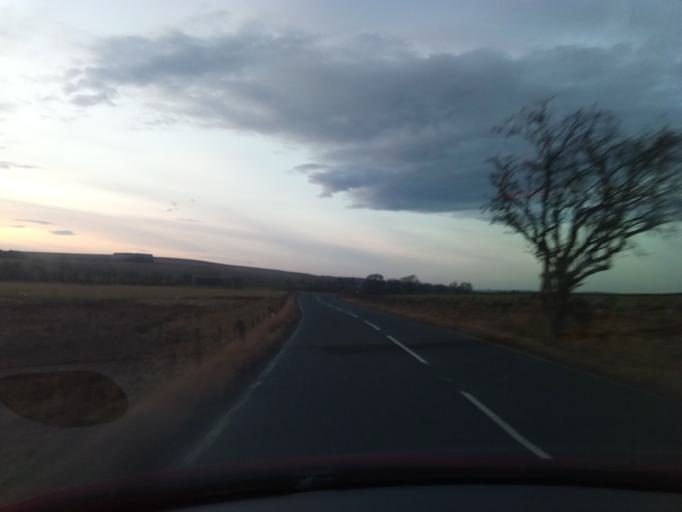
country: GB
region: England
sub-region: Northumberland
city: Otterburn
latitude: 55.2405
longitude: -2.2091
